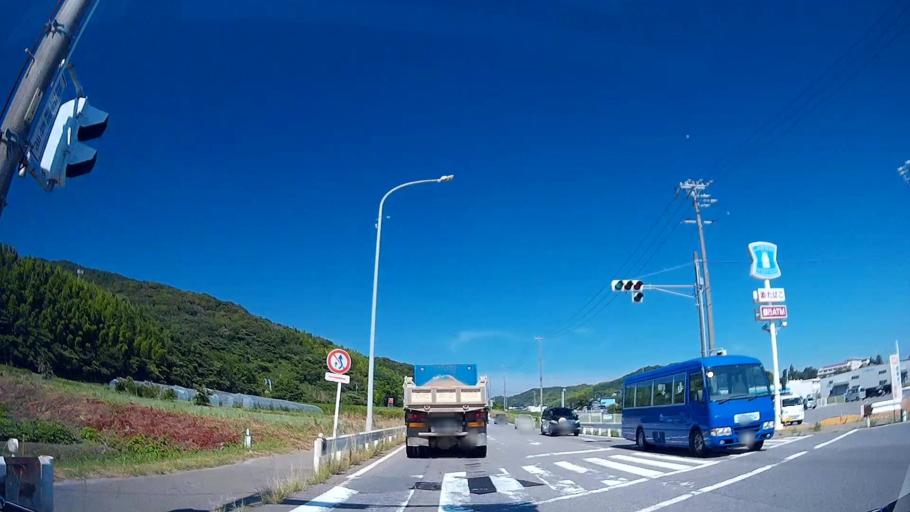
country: JP
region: Aichi
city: Gamagori
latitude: 34.8304
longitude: 137.1802
